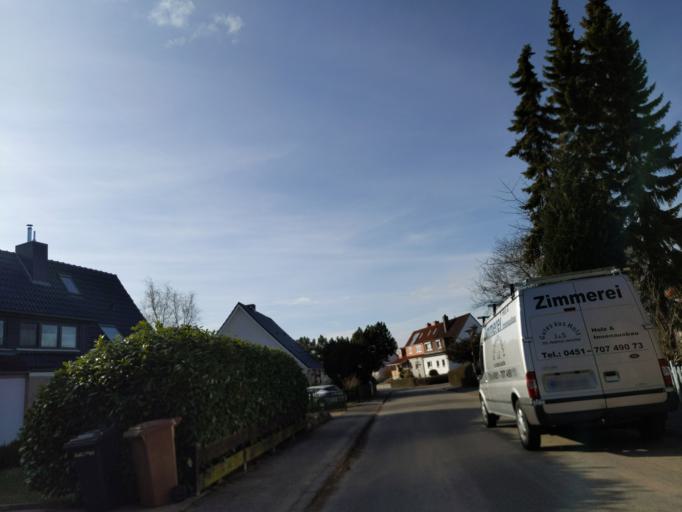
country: DE
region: Schleswig-Holstein
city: Travemuende
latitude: 53.9569
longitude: 10.8449
